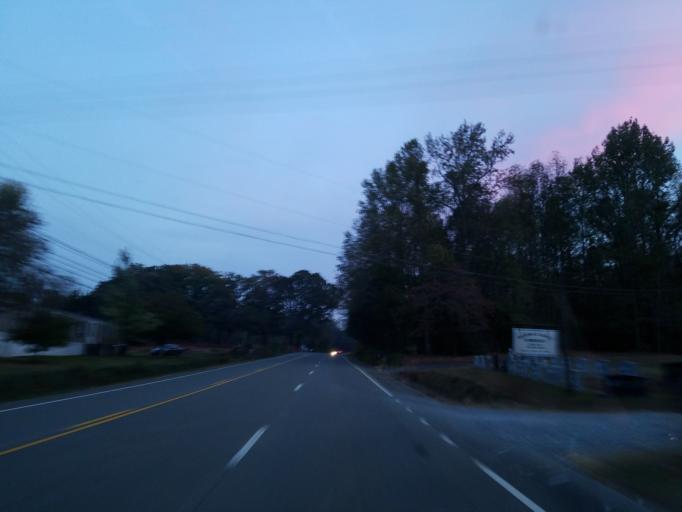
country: US
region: Georgia
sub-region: Pickens County
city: Jasper
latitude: 34.4962
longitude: -84.4705
